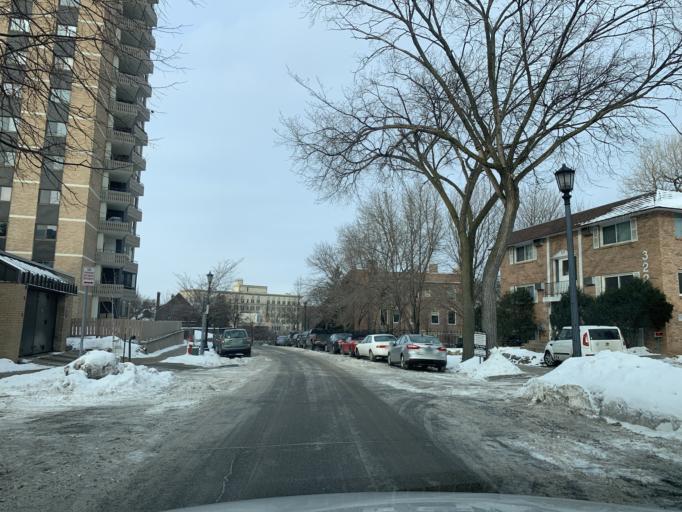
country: US
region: Minnesota
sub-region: Hennepin County
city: Minneapolis
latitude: 44.9662
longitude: -93.2843
